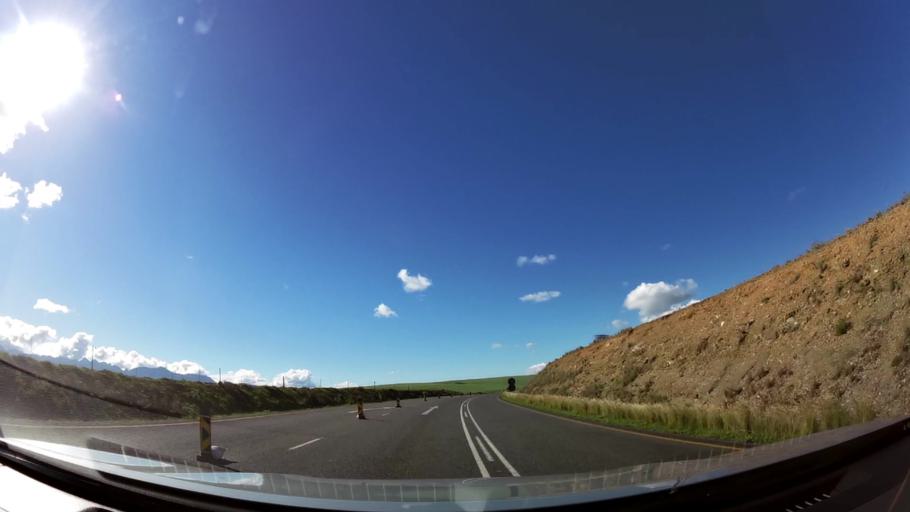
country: ZA
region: Western Cape
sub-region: Overberg District Municipality
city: Caledon
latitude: -34.1824
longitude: 19.6897
